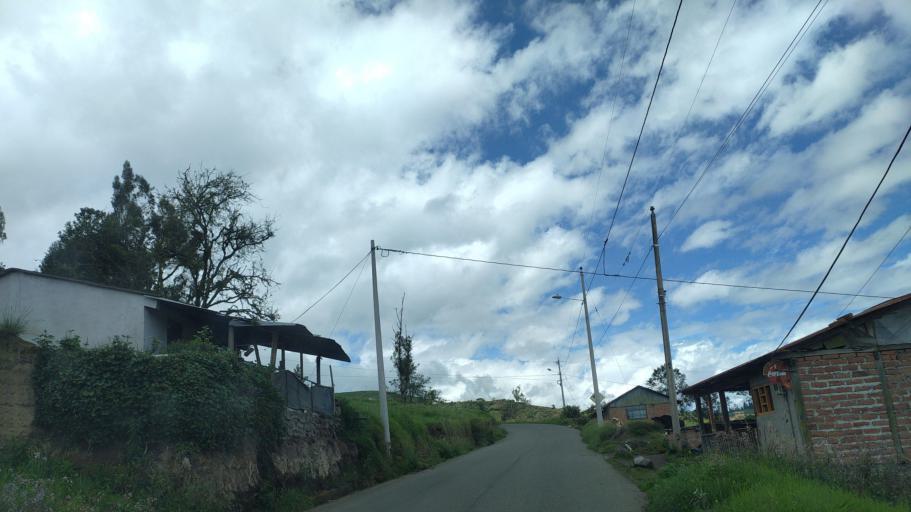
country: EC
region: Chimborazo
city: Riobamba
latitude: -1.6685
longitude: -78.5702
